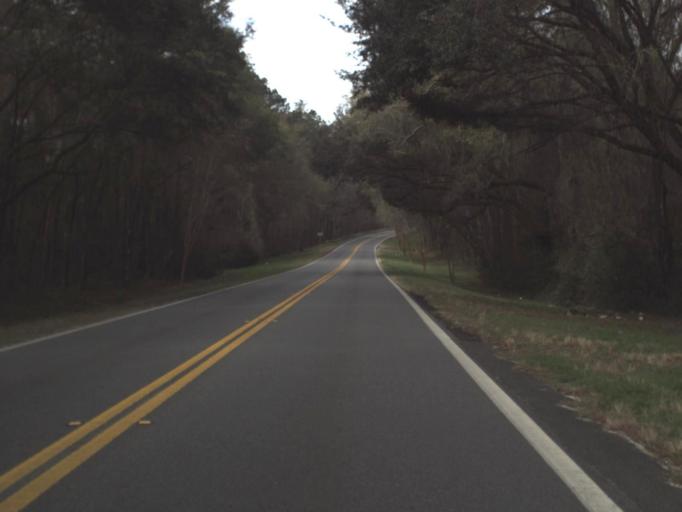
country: US
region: Florida
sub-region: Jefferson County
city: Monticello
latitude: 30.5195
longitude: -84.0383
